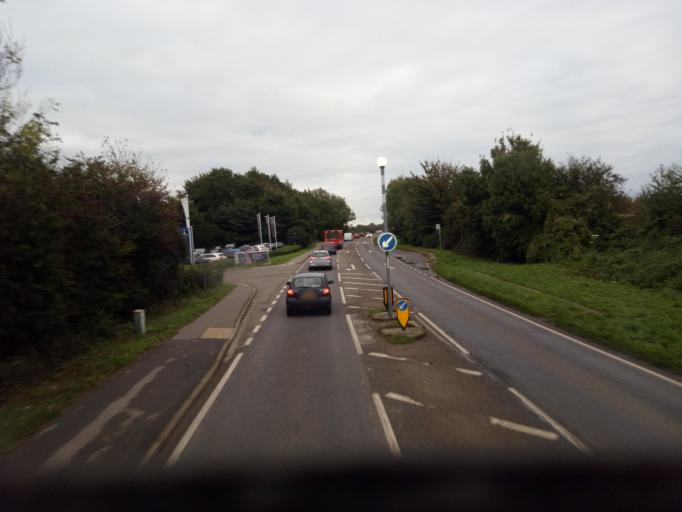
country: GB
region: England
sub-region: West Sussex
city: Boxgrove
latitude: 50.8200
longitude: -0.7166
